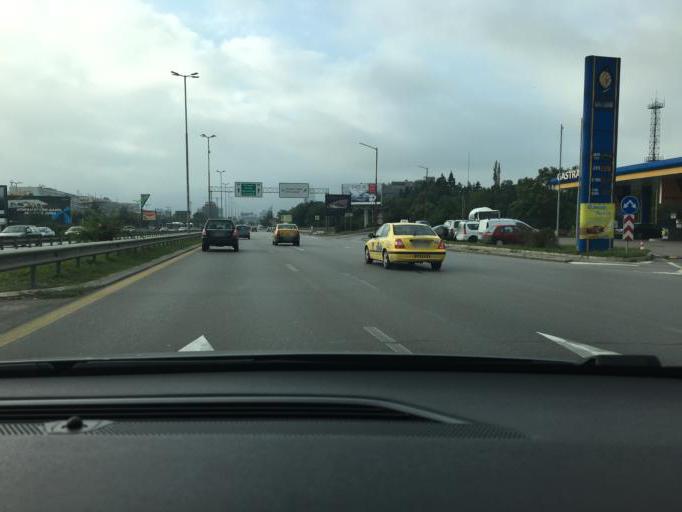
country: BG
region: Sofia-Capital
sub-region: Stolichna Obshtina
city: Sofia
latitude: 42.6581
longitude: 23.3831
